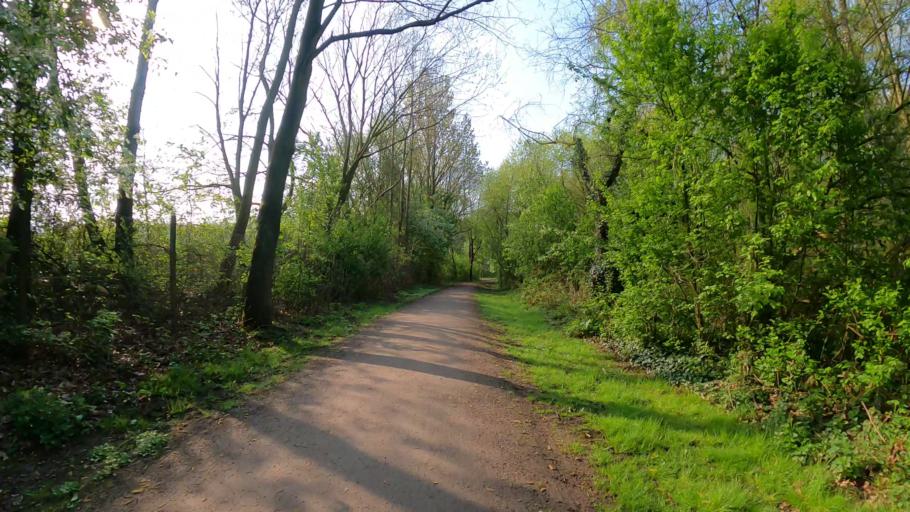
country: DE
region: Hamburg
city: Kleiner Grasbrook
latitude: 53.5128
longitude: 10.0127
